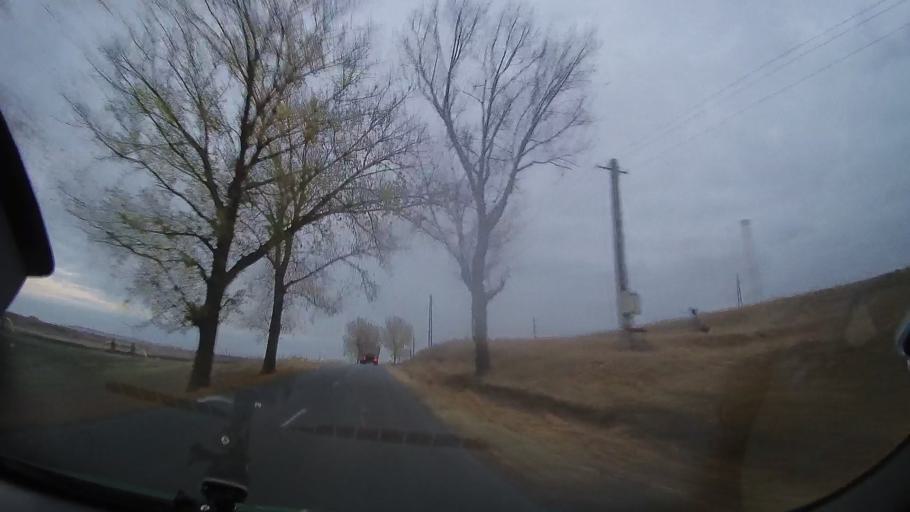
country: RO
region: Tulcea
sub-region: Comuna Mihai Bravu
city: Mihai Bravu
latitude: 44.9598
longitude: 28.6448
